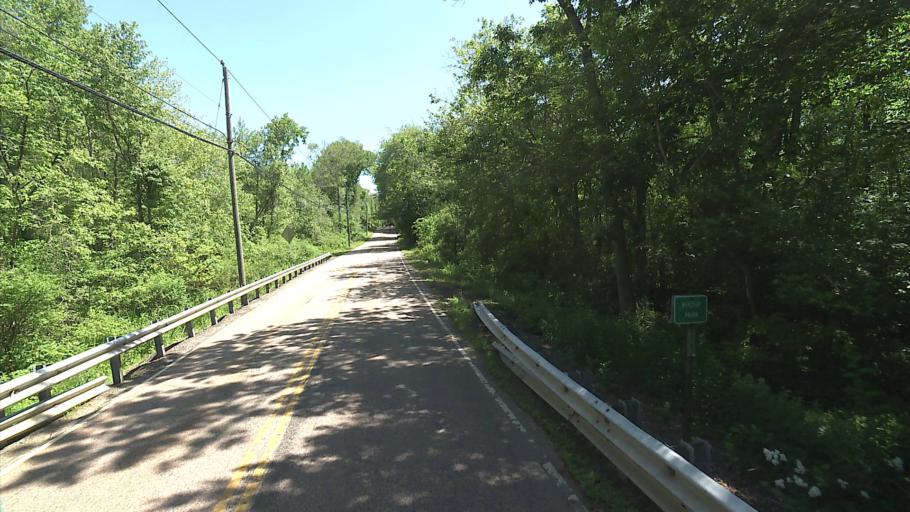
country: US
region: Rhode Island
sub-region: Washington County
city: Ashaway
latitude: 41.4513
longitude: -71.8452
